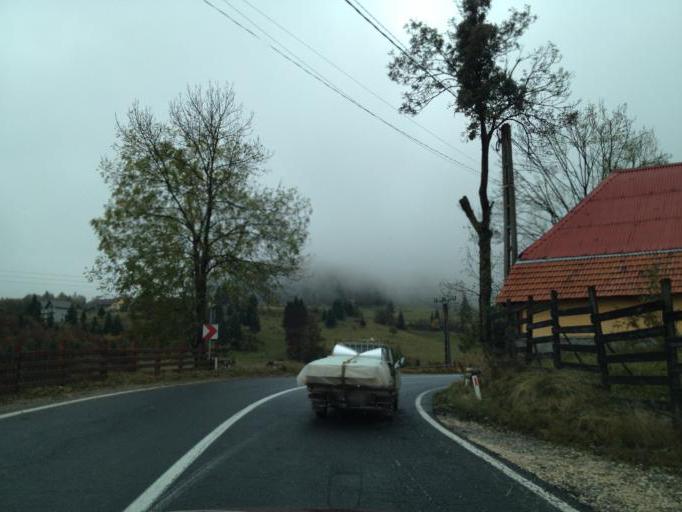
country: RO
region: Brasov
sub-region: Comuna Fundata
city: Fundata
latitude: 45.4500
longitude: 25.2747
